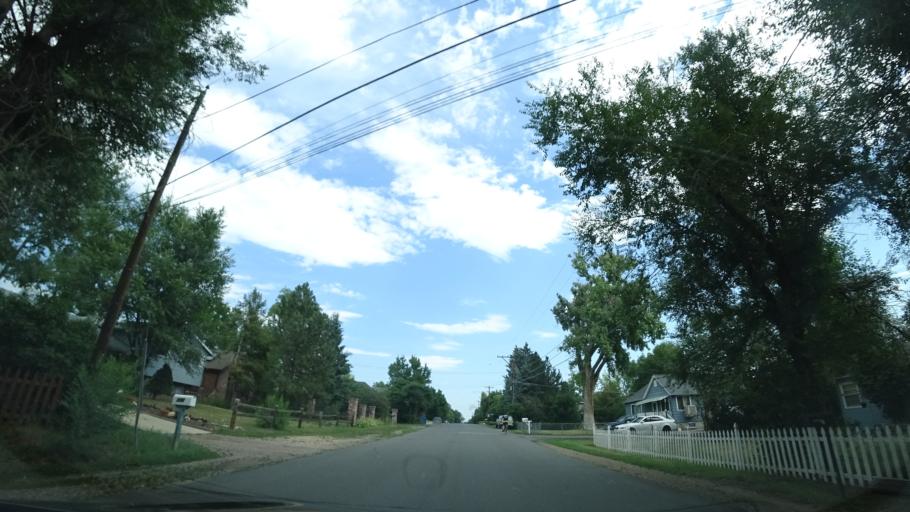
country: US
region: Colorado
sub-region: Jefferson County
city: Lakewood
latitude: 39.7207
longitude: -105.0698
